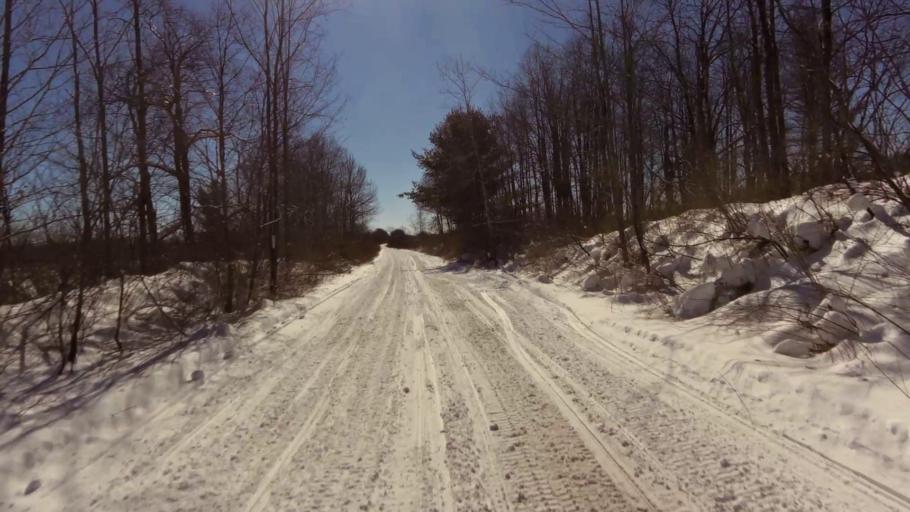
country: US
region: New York
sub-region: Chautauqua County
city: Mayville
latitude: 42.1797
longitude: -79.5811
